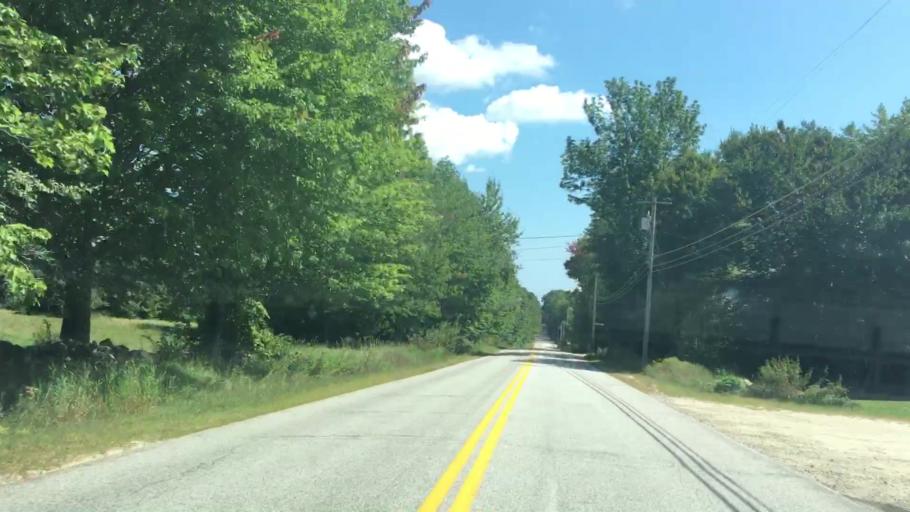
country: US
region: Maine
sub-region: Cumberland County
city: New Gloucester
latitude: 43.9413
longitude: -70.2978
